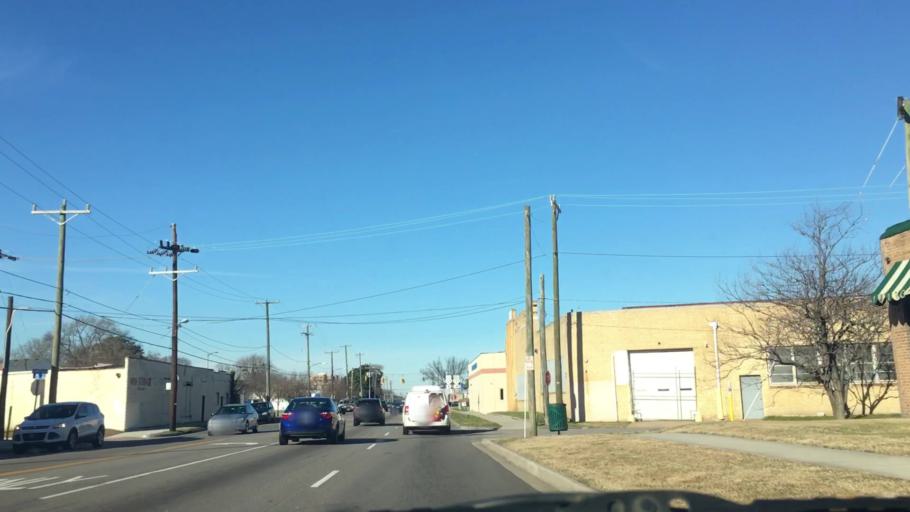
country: US
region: Virginia
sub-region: City of Norfolk
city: Norfolk
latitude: 36.8752
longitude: -76.3018
